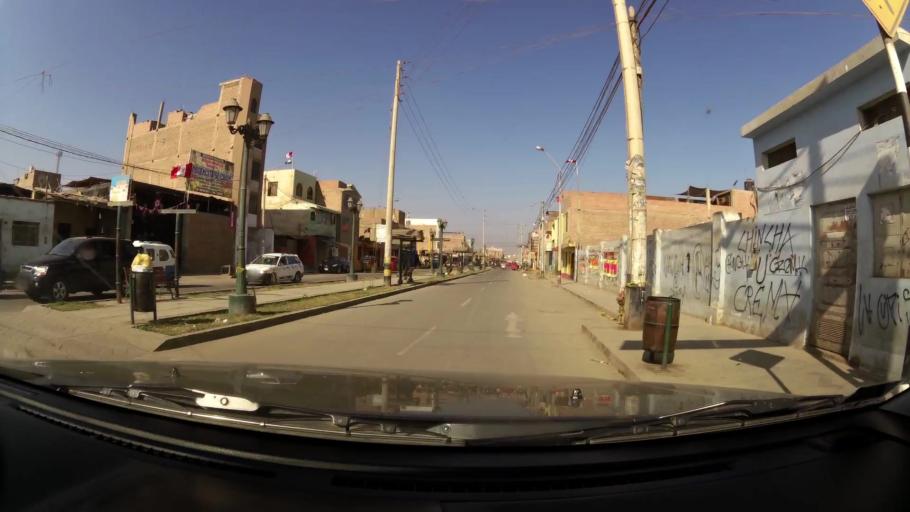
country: PE
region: Ica
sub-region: Provincia de Chincha
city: Chincha Alta
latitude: -13.4153
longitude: -76.1393
